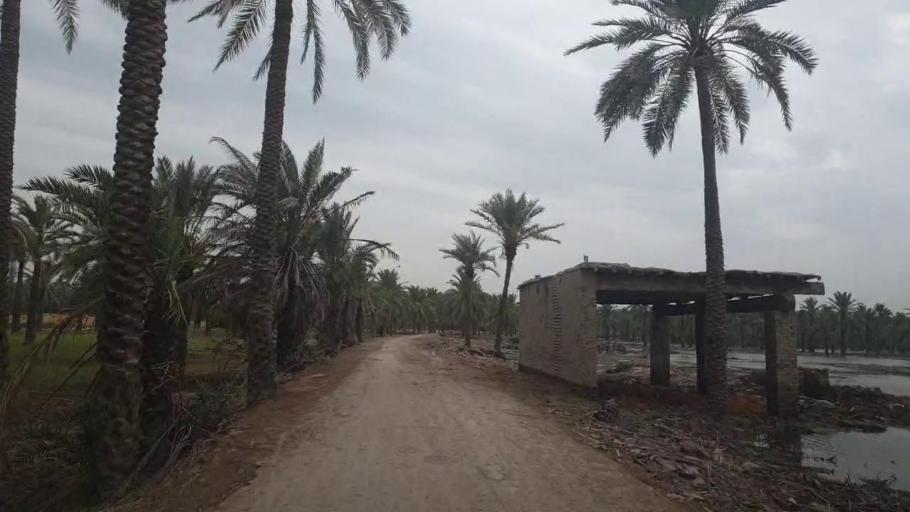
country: PK
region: Sindh
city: Khairpur
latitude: 27.5872
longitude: 68.7497
